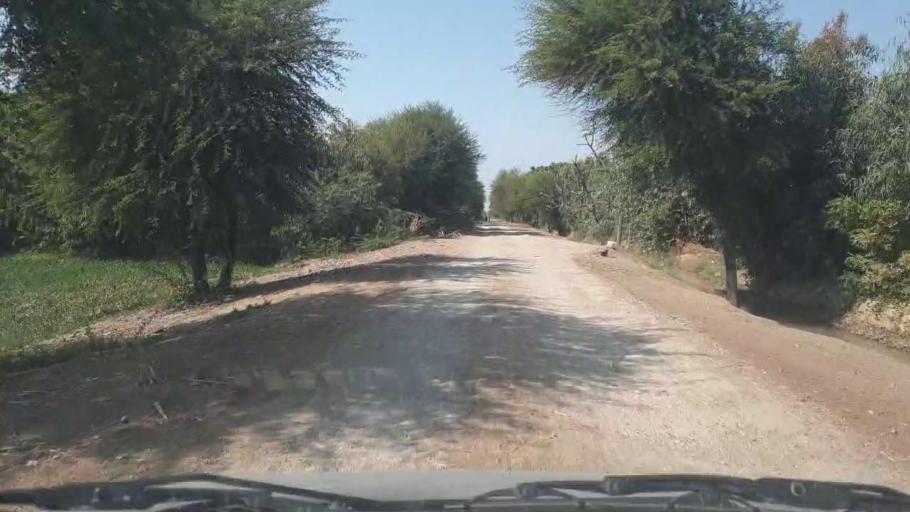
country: PK
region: Sindh
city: Samaro
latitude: 25.2370
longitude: 69.3285
